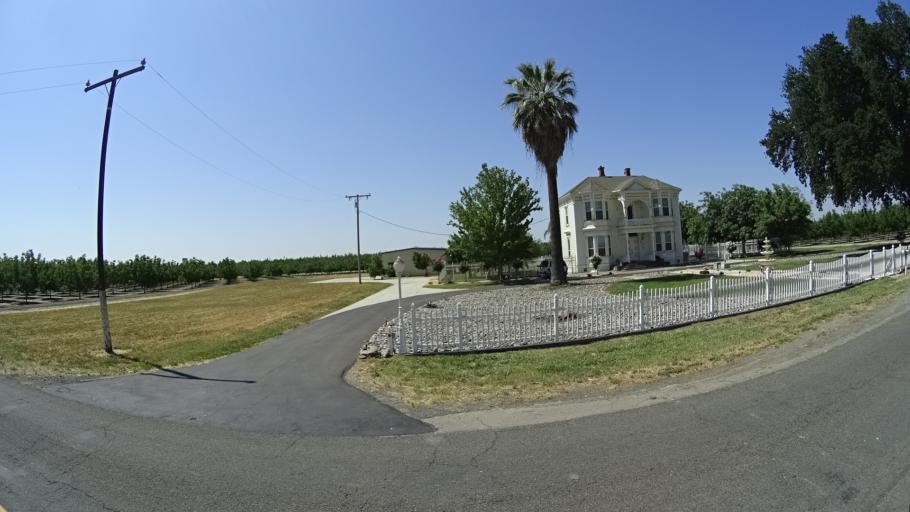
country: US
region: California
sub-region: Kings County
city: Lucerne
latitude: 36.3716
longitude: -119.6071
